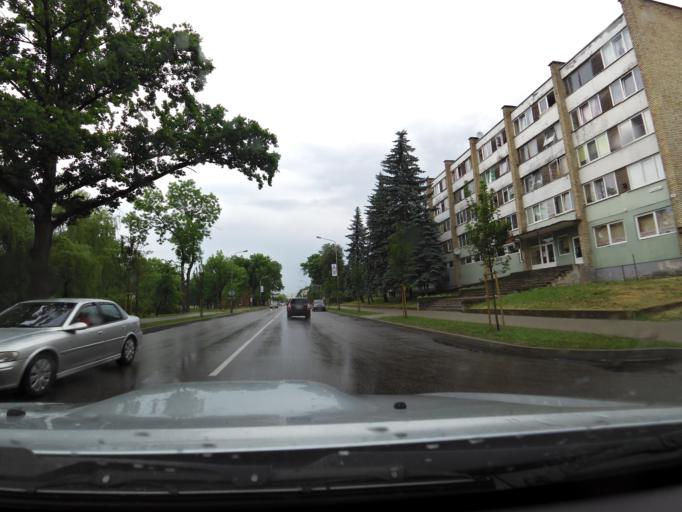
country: LT
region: Marijampoles apskritis
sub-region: Marijampole Municipality
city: Marijampole
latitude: 54.5496
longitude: 23.3480
